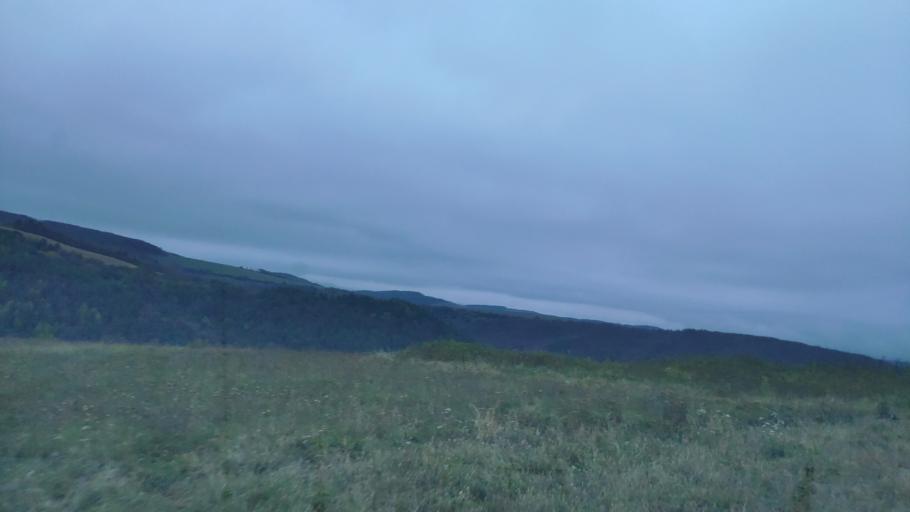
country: SK
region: Presovsky
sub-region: Okres Presov
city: Presov
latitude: 48.9374
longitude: 21.0854
